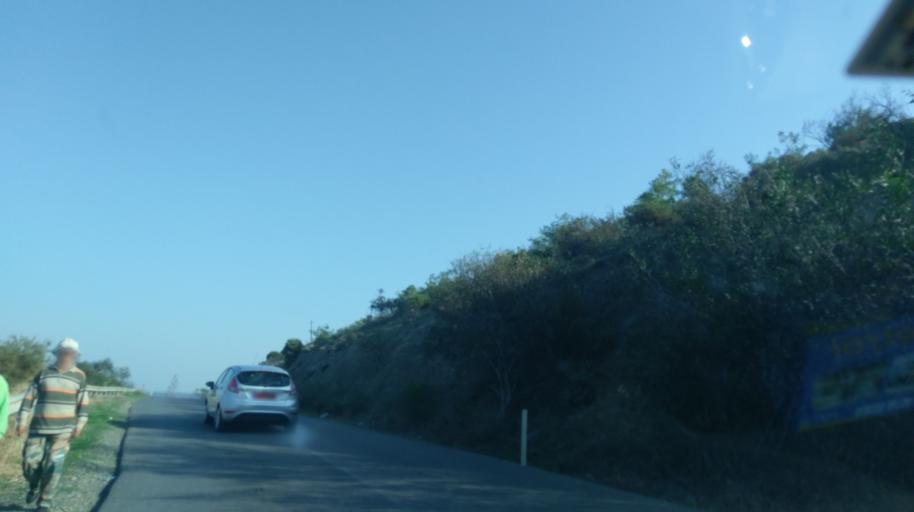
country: CY
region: Lefkosia
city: Lefka
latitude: 35.1518
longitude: 32.7931
